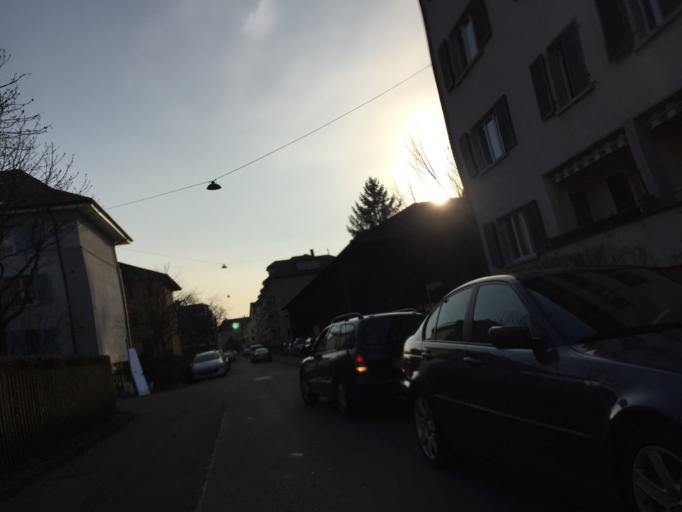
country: CH
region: Bern
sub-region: Bern-Mittelland District
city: Bern
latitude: 46.9626
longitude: 7.4507
